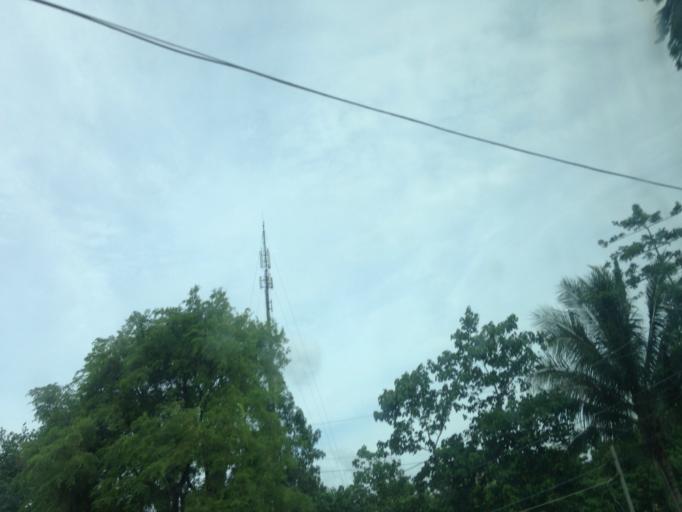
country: PH
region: Mimaropa
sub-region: Province of Mindoro Oriental
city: Manaul
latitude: 12.4464
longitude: 121.4069
